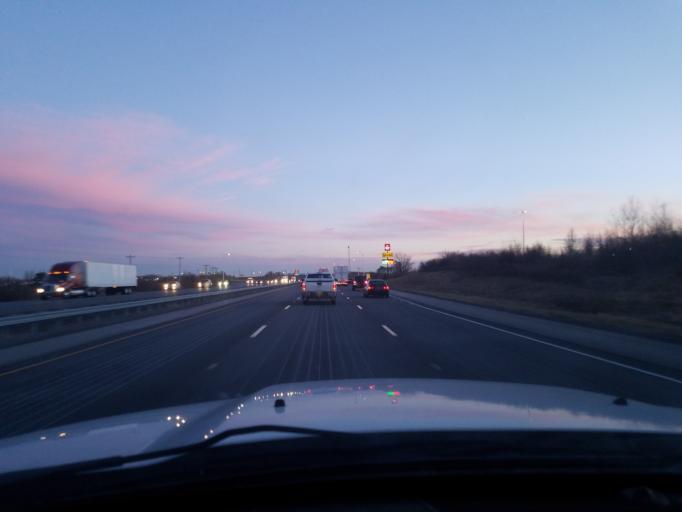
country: US
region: Indiana
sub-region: Johnson County
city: Whiteland
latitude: 39.5558
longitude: -86.0449
